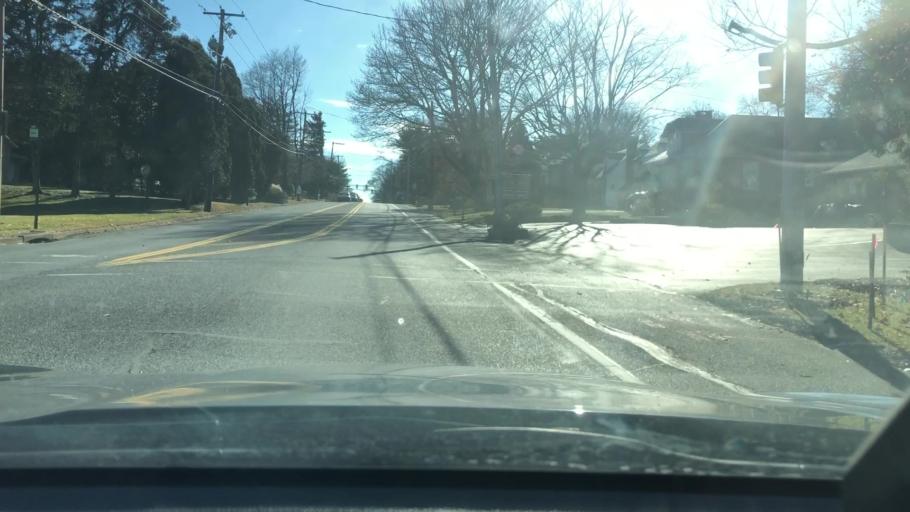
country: US
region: Pennsylvania
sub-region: Northampton County
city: Bethlehem
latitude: 40.6566
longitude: -75.3781
